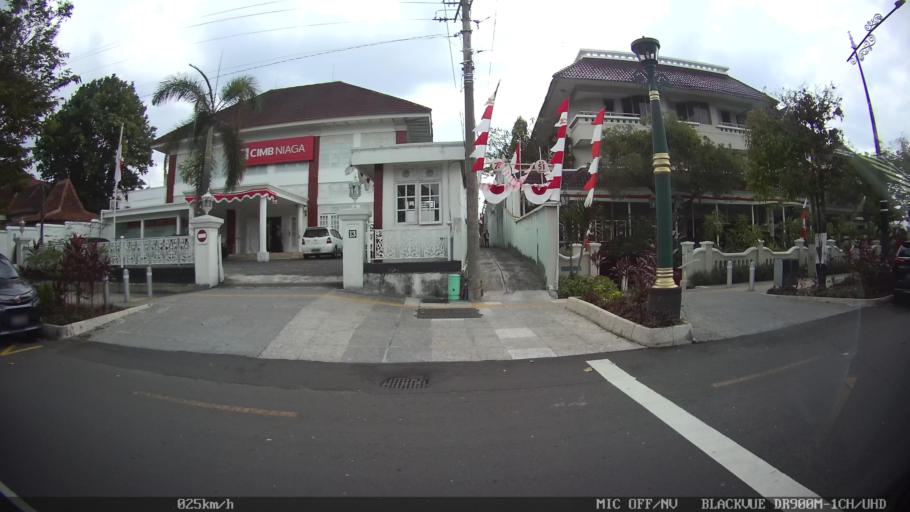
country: ID
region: Daerah Istimewa Yogyakarta
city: Yogyakarta
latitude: -7.7833
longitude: 110.3684
